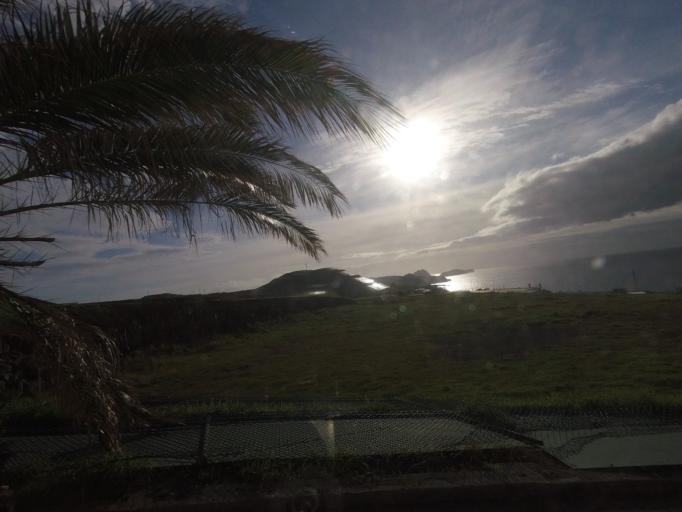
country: PT
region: Madeira
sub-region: Machico
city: Canical
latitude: 32.7440
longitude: -16.7382
